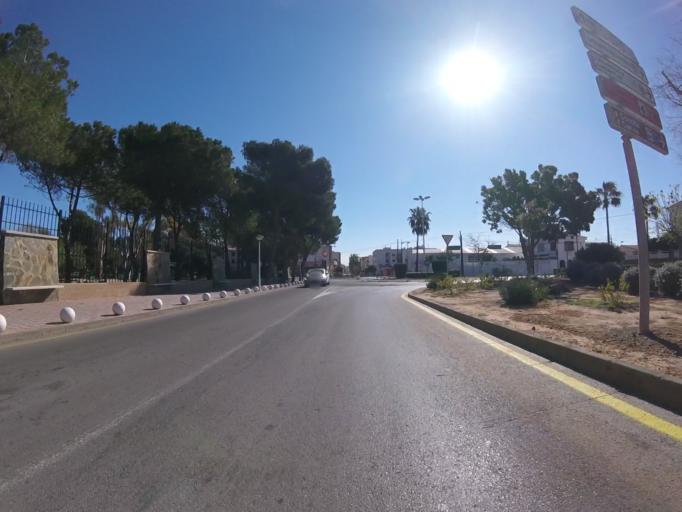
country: ES
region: Valencia
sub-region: Provincia de Castello
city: Orpesa/Oropesa del Mar
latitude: 40.0923
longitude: 0.1313
